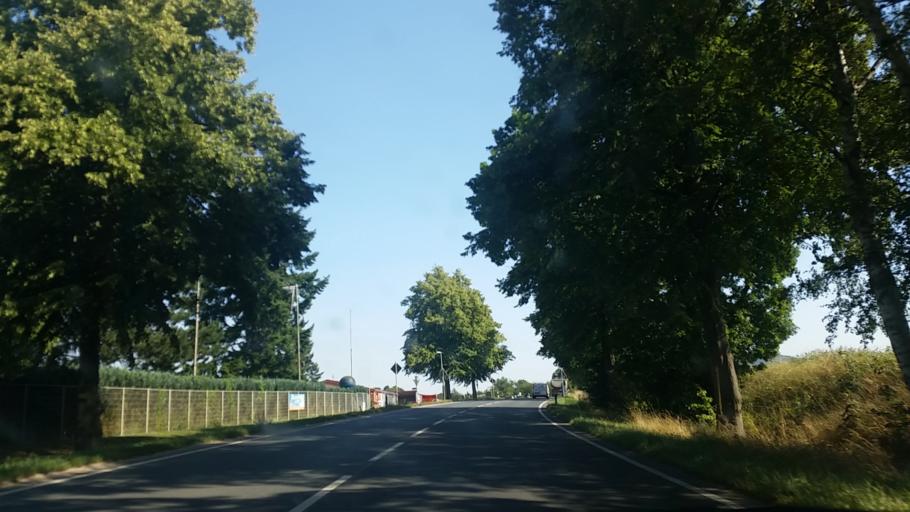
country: DE
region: Lower Saxony
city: Coppenbrugge
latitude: 52.1035
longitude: 9.5768
